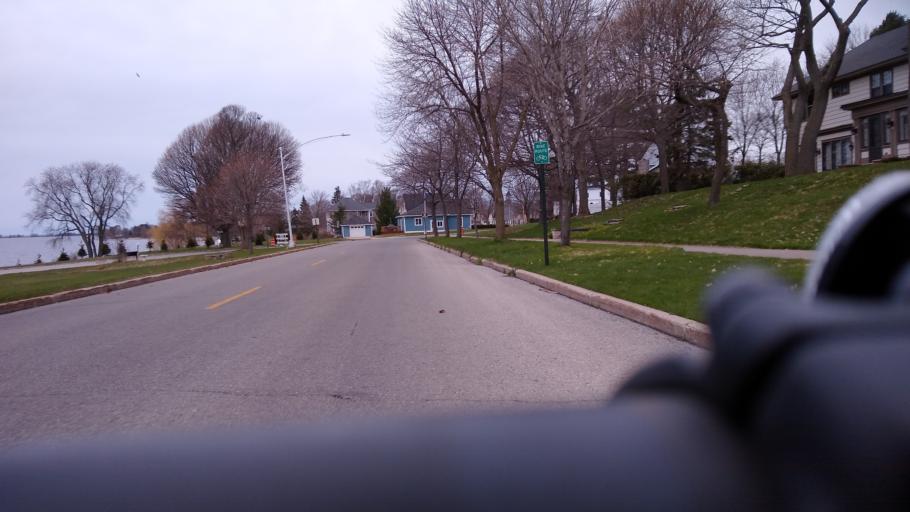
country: US
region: Michigan
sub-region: Delta County
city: Escanaba
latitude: 45.7380
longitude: -87.0575
